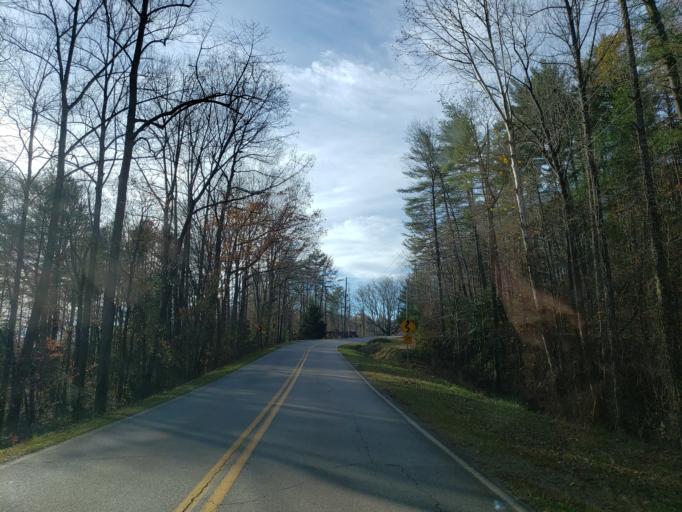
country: US
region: Georgia
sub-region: Lumpkin County
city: Dahlonega
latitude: 34.6048
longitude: -84.0640
